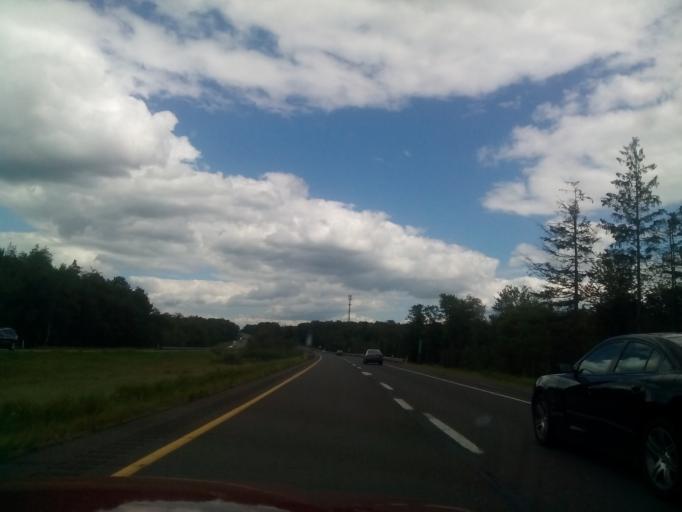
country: US
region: Pennsylvania
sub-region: Monroe County
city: Emerald Lakes
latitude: 41.0711
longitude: -75.4453
